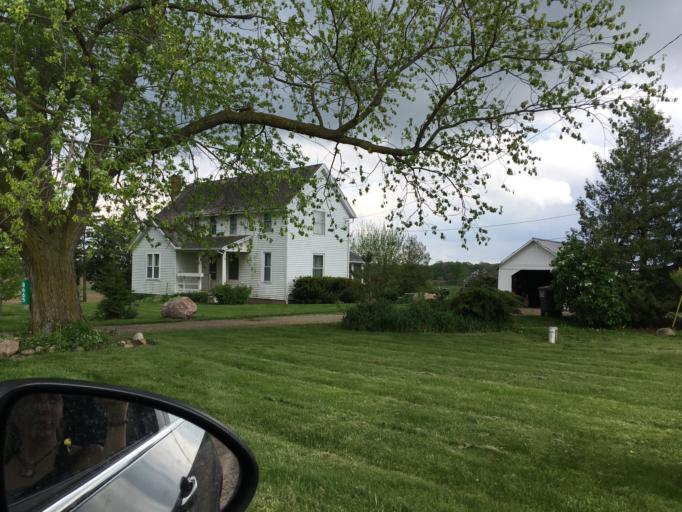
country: US
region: Michigan
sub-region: Washtenaw County
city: Saline
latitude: 42.1893
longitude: -83.8971
